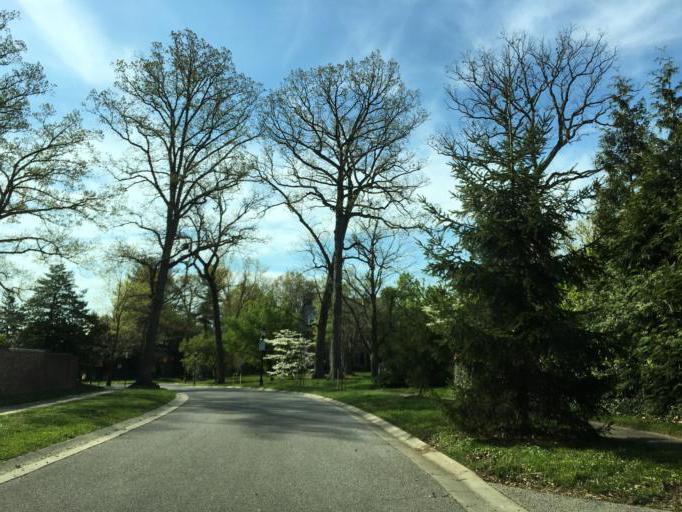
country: US
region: Maryland
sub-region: City of Baltimore
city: Baltimore
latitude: 39.3438
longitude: -76.6193
